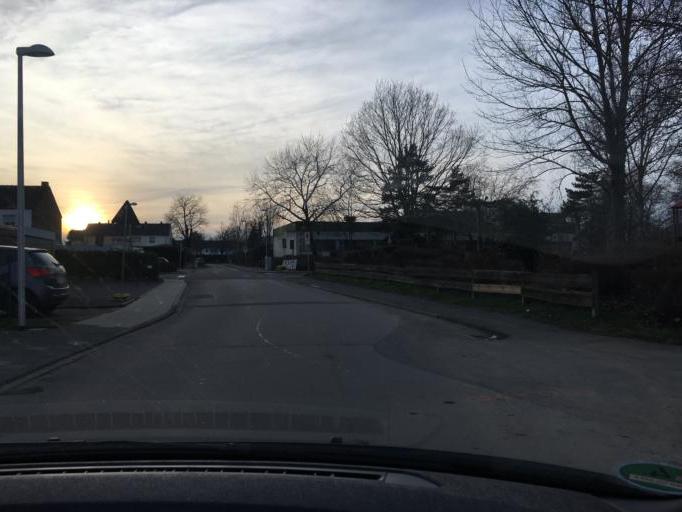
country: DE
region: North Rhine-Westphalia
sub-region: Regierungsbezirk Koln
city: Dueren
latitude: 50.7934
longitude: 6.5057
